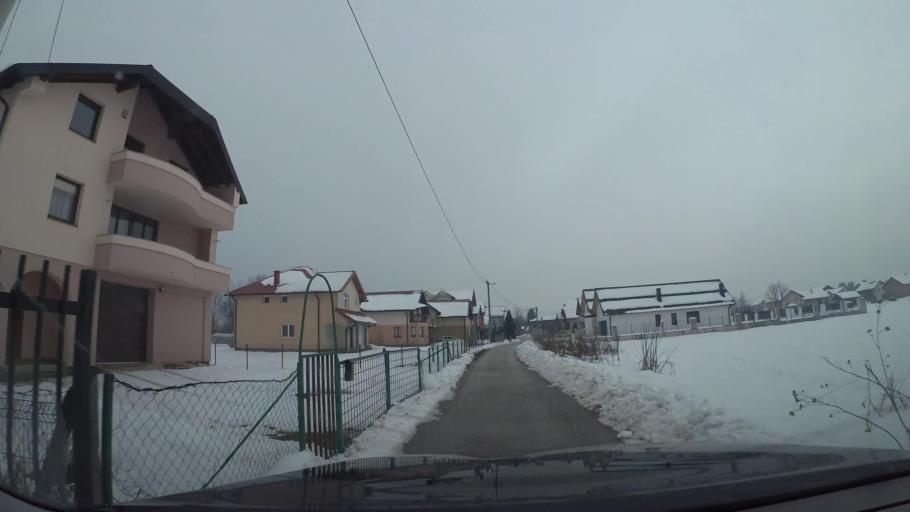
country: BA
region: Federation of Bosnia and Herzegovina
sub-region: Kanton Sarajevo
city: Sarajevo
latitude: 43.8422
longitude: 18.3029
